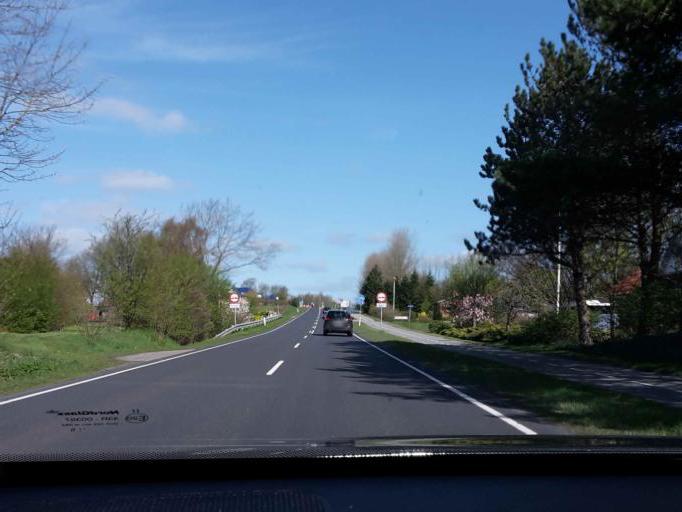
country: DK
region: South Denmark
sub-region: Vejen Kommune
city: Vejen
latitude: 55.5199
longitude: 9.1205
